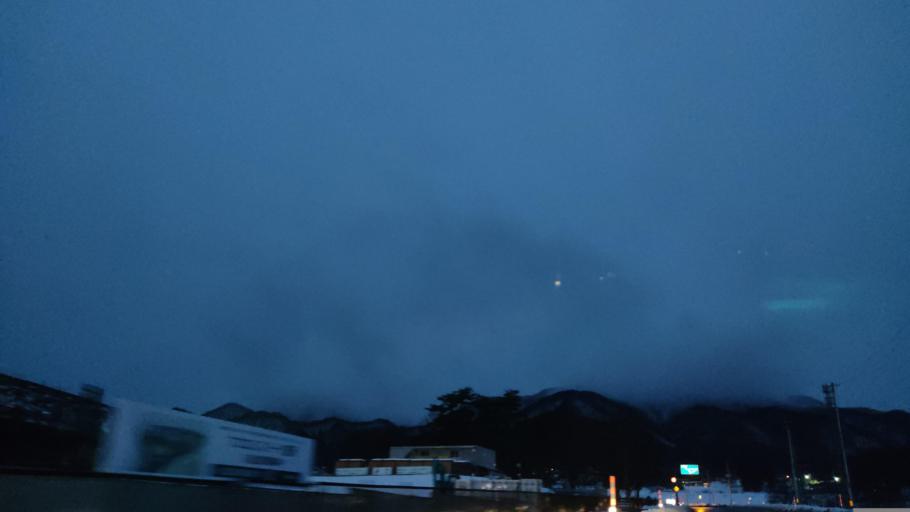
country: JP
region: Iwate
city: Morioka-shi
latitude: 39.6319
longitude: 141.1004
